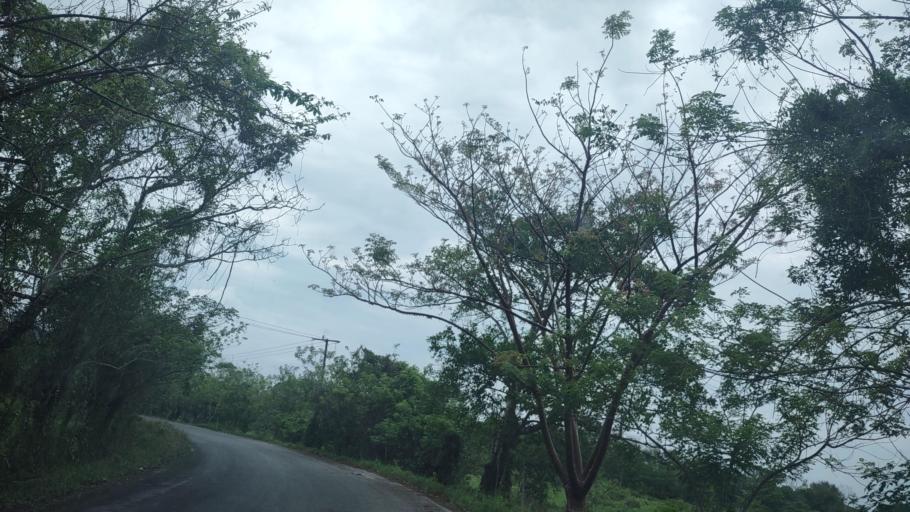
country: MX
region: Tabasco
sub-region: Huimanguillo
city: Francisco Rueda
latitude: 17.5270
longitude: -94.1242
